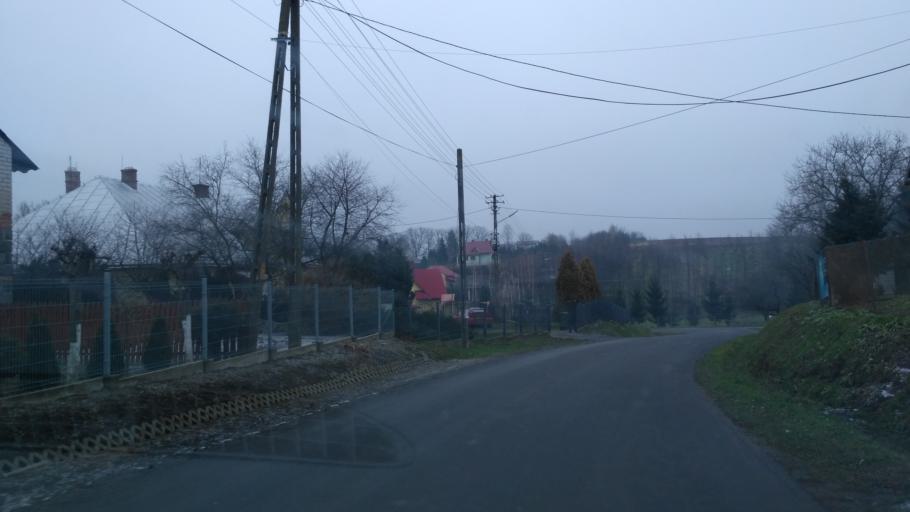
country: PL
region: Subcarpathian Voivodeship
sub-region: Powiat przeworski
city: Zarzecze
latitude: 49.9606
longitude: 22.5674
